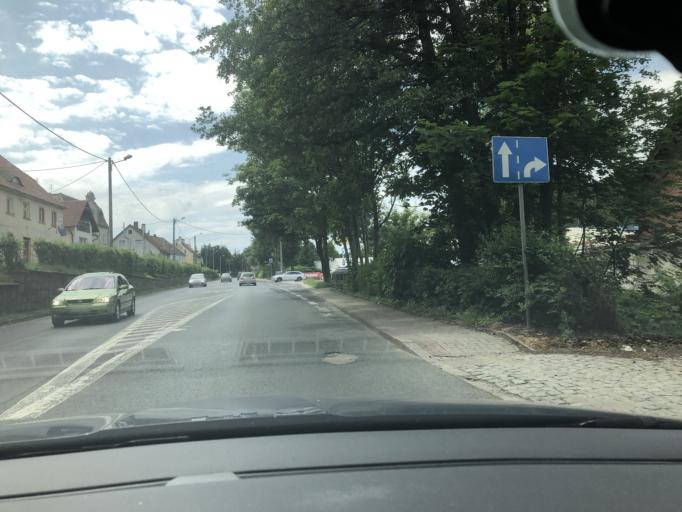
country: PL
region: Lower Silesian Voivodeship
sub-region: Powiat zlotoryjski
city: Zlotoryja
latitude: 51.1287
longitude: 15.9278
